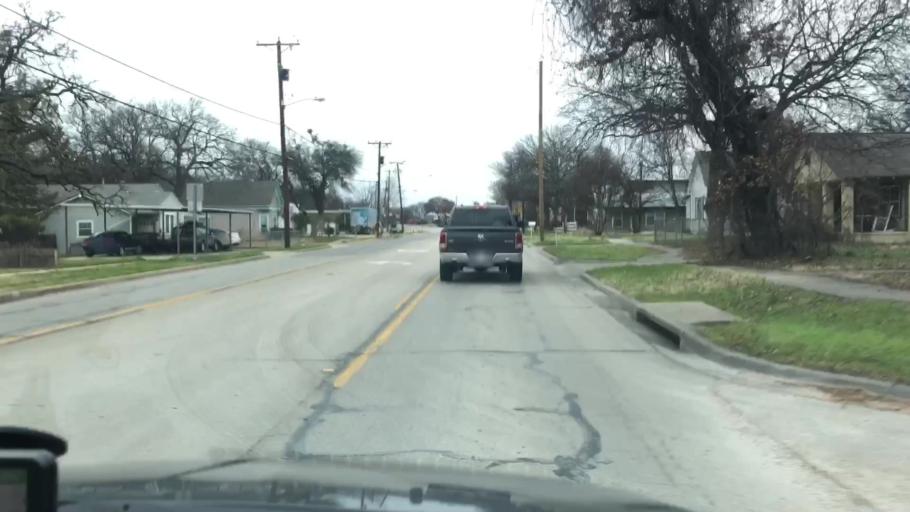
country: US
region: Texas
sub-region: Palo Pinto County
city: Mineral Wells
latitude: 32.8229
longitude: -98.1128
